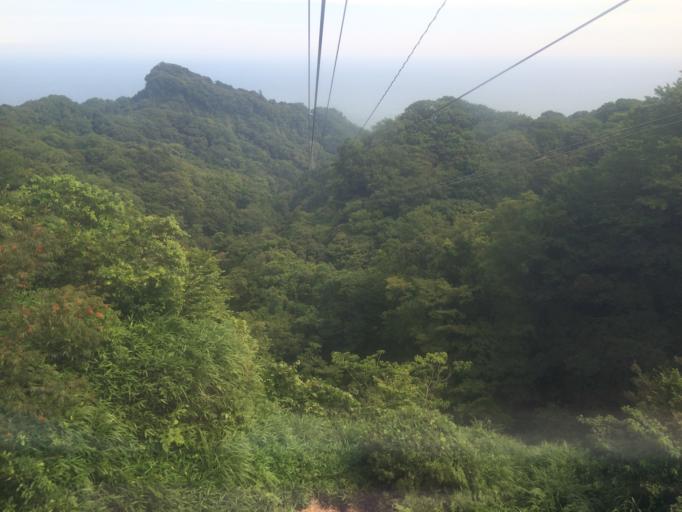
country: JP
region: Shizuoka
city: Shizuoka-shi
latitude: 34.9730
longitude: 138.4641
